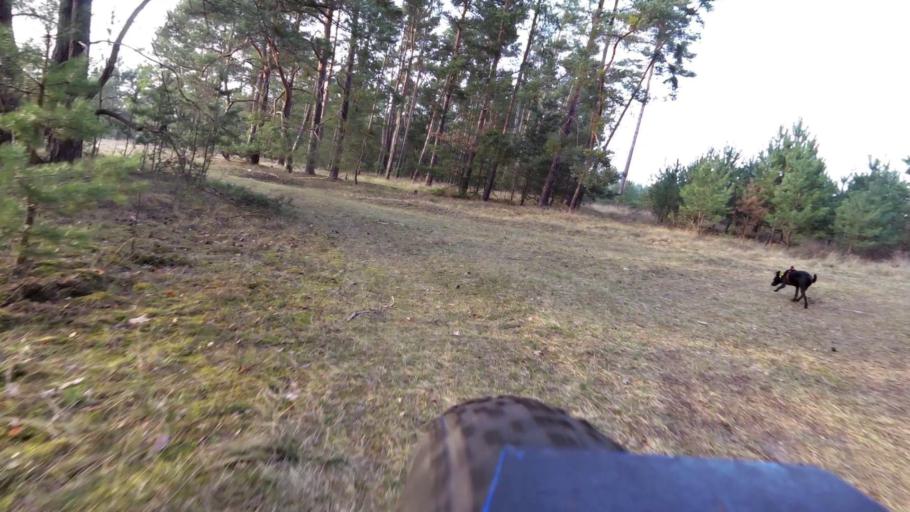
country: DE
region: Brandenburg
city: Ziltendorf
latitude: 52.2712
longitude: 14.6887
